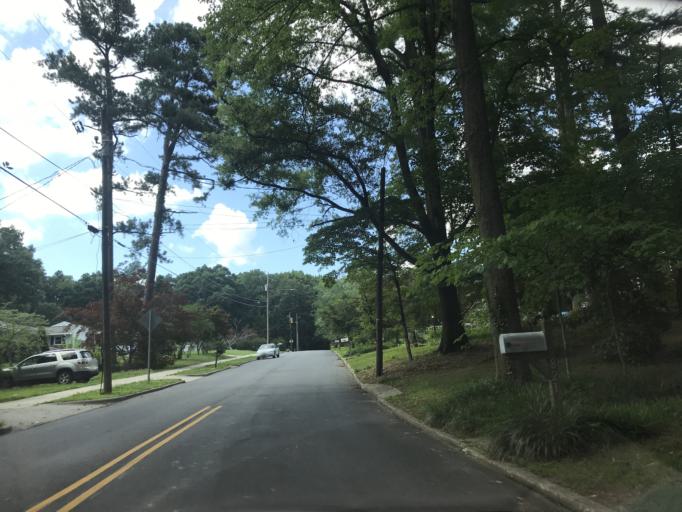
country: US
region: North Carolina
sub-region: Wake County
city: West Raleigh
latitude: 35.7784
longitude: -78.7164
